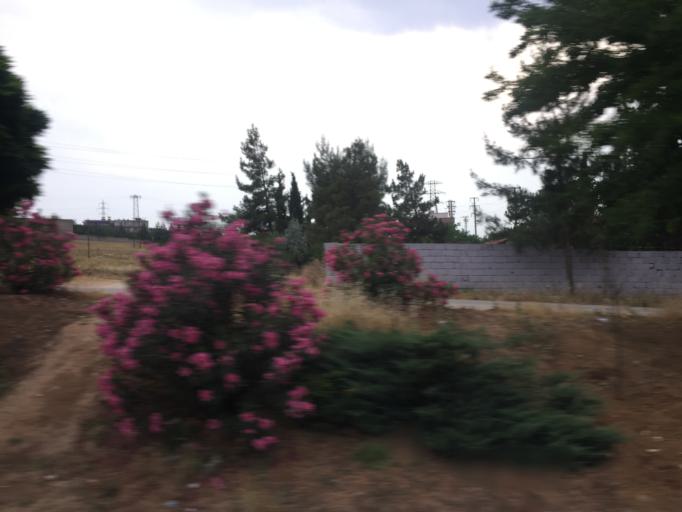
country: TR
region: Gaziantep
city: Gaziantep
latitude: 37.0188
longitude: 37.4294
